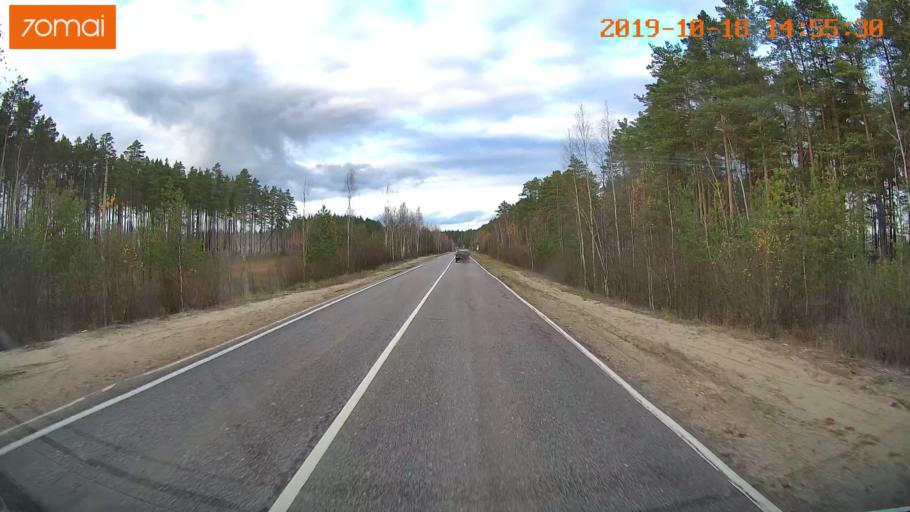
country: RU
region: Vladimir
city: Kurlovo
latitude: 55.4531
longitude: 40.5890
